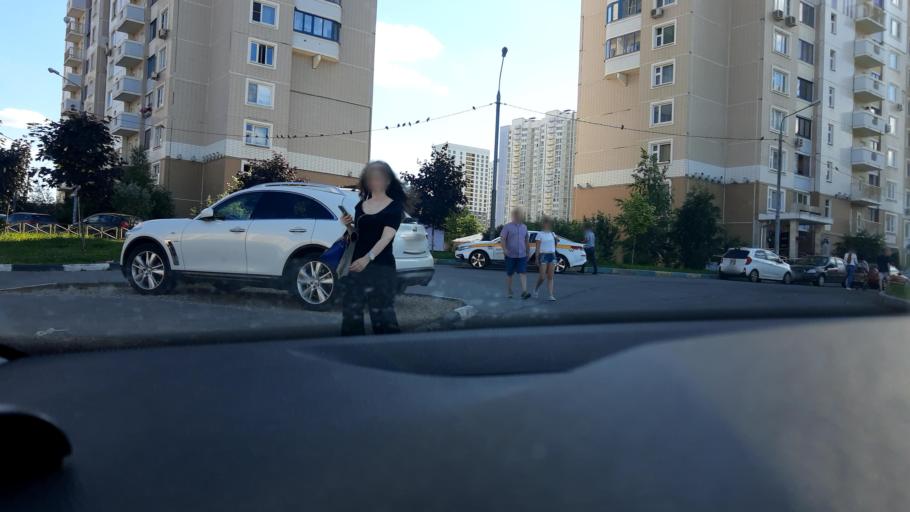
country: RU
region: Moscow
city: Khimki
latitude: 55.9071
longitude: 37.3975
